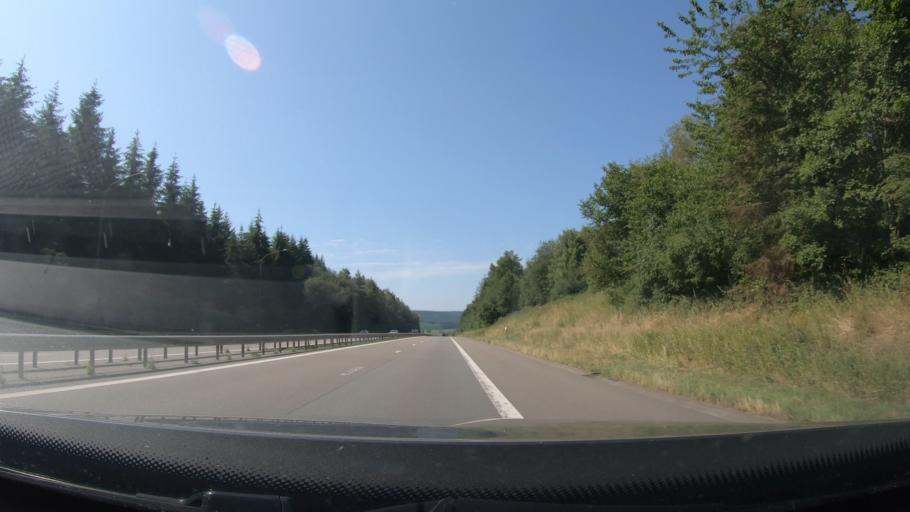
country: BE
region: Wallonia
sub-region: Province de Liege
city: Malmedy
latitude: 50.4037
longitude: 5.9860
